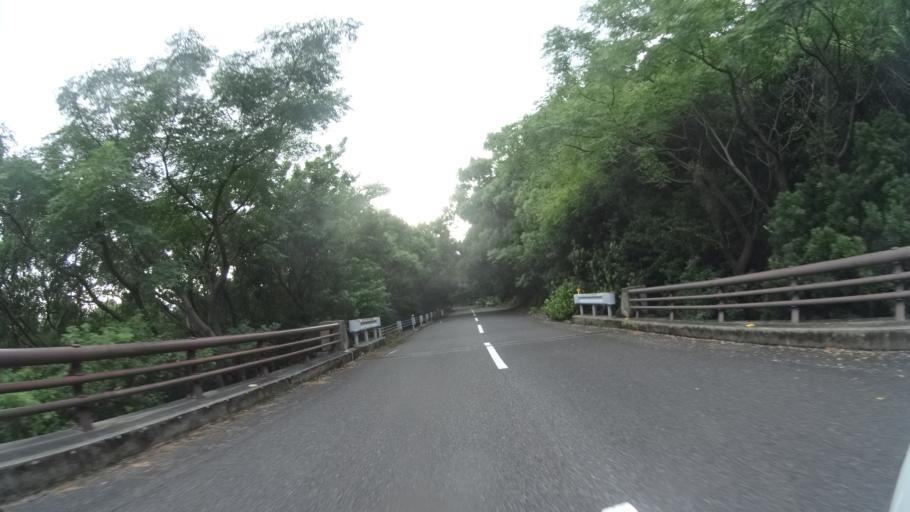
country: JP
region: Kagoshima
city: Nishinoomote
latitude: 30.3193
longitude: 130.3998
